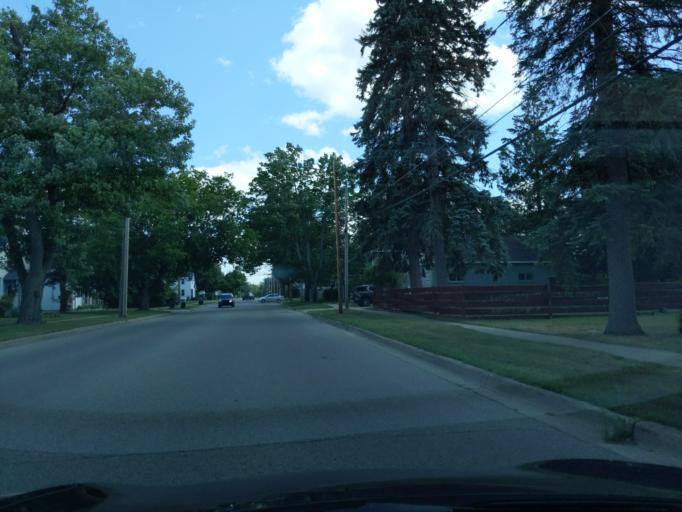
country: US
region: Michigan
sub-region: Crawford County
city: Grayling
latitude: 44.6656
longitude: -84.7136
